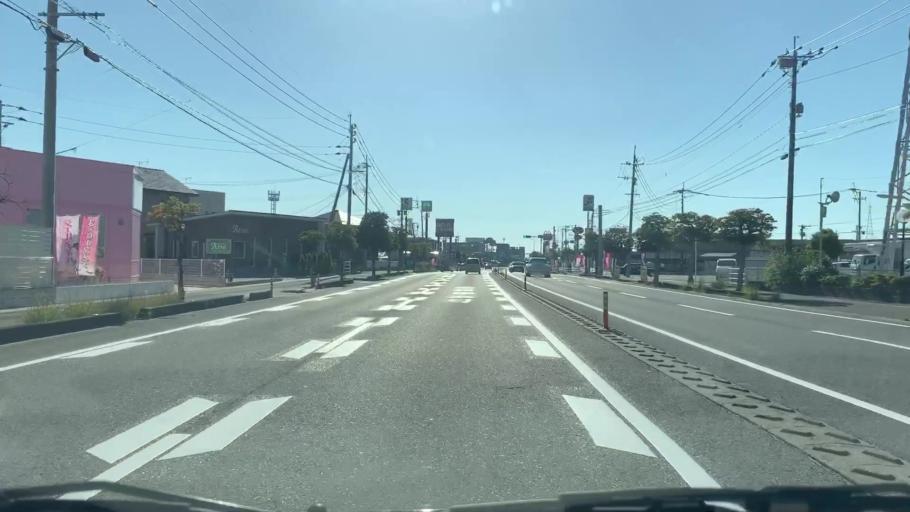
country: JP
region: Saga Prefecture
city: Saga-shi
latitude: 33.2955
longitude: 130.2831
